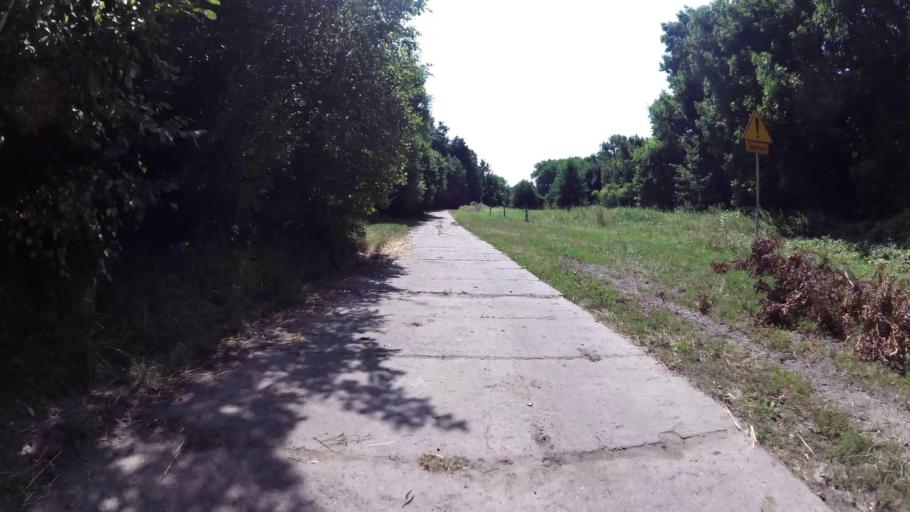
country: PL
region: West Pomeranian Voivodeship
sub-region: Powiat stargardzki
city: Suchan
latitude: 53.2576
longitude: 15.3985
